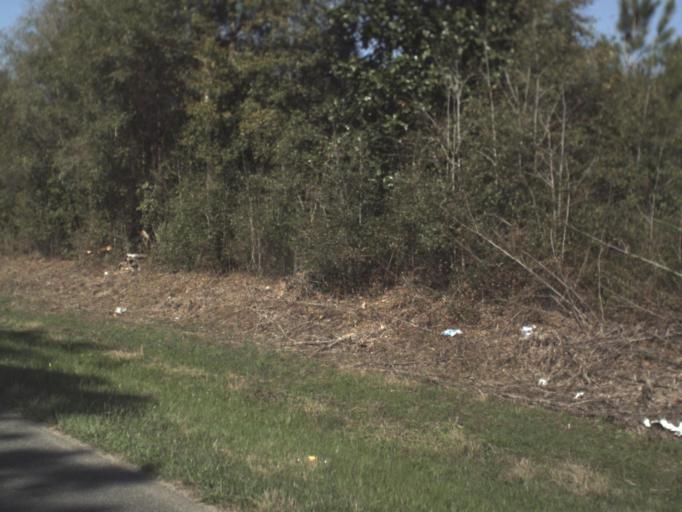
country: US
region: Florida
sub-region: Jackson County
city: Marianna
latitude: 30.6926
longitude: -85.1800
